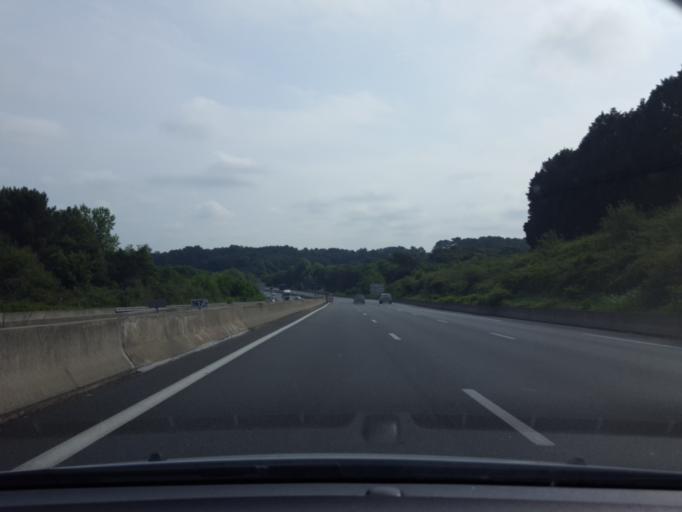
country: FR
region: Aquitaine
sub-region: Departement des Pyrenees-Atlantiques
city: Boucau
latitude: 43.5281
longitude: -1.4366
